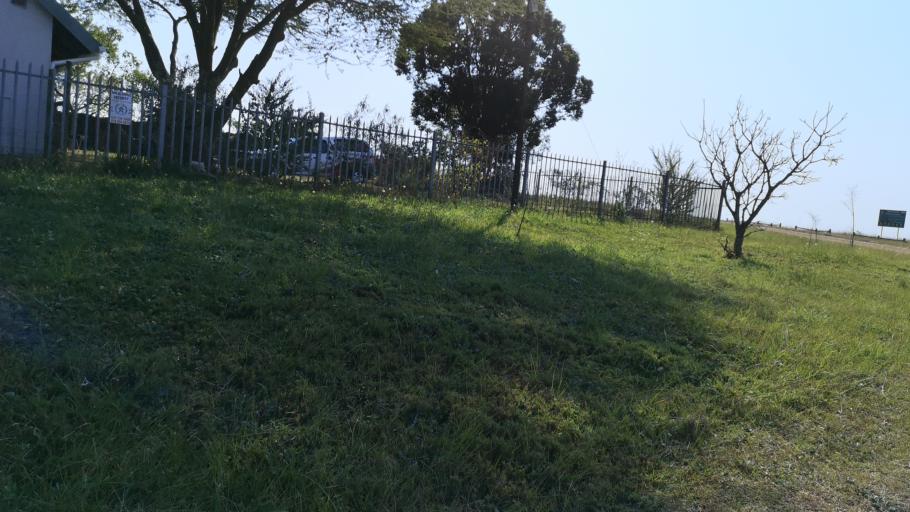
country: ZA
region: KwaZulu-Natal
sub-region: eThekwini Metropolitan Municipality
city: Mpumalanga
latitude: -29.7360
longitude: 30.6855
